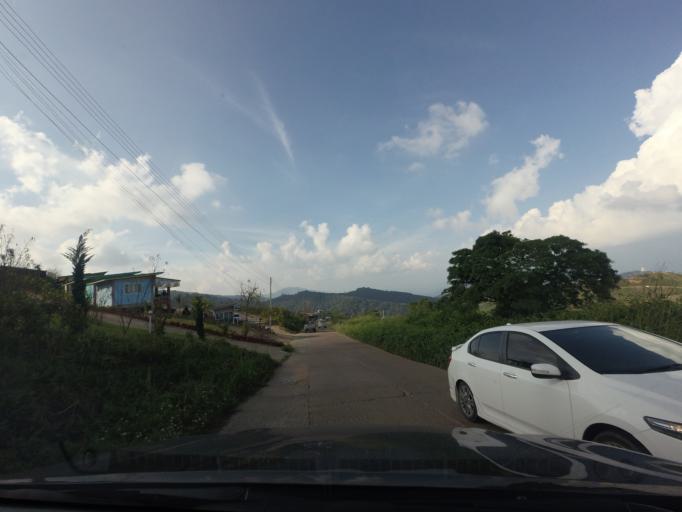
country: TH
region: Phetchabun
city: Lom Kao
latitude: 16.9013
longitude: 101.1058
